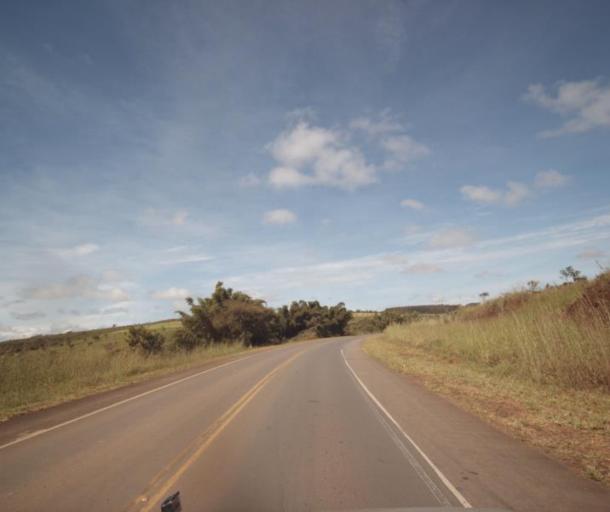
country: BR
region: Goias
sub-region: Anapolis
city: Anapolis
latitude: -16.1584
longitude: -48.8884
